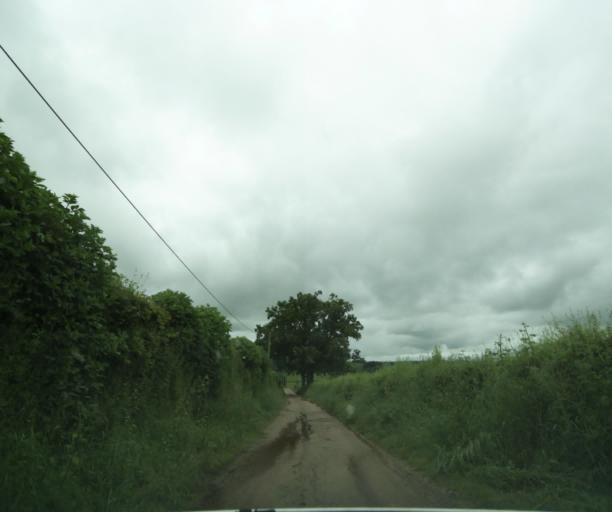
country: FR
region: Bourgogne
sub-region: Departement de Saone-et-Loire
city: Charolles
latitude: 46.4750
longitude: 4.3501
